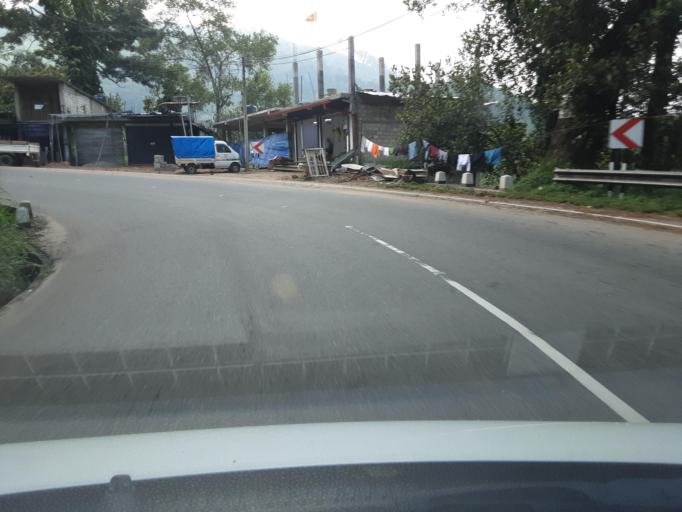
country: LK
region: Uva
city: Badulla
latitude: 6.9543
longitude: 81.0266
